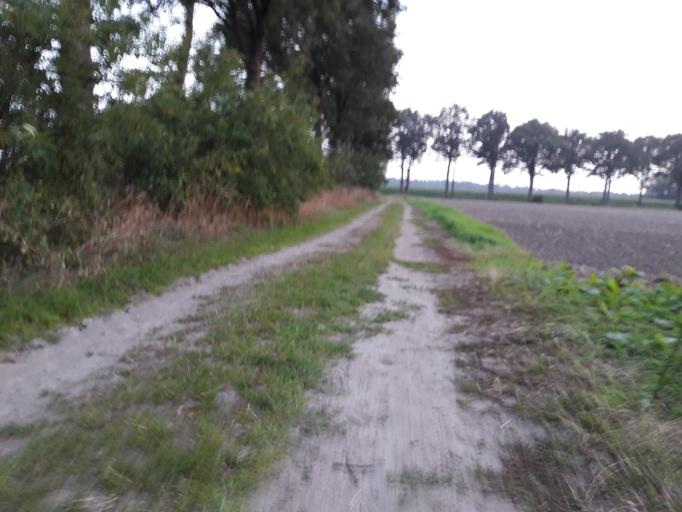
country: NL
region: Drenthe
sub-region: Gemeente Borger-Odoorn
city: Borger
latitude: 52.9539
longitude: 6.8132
